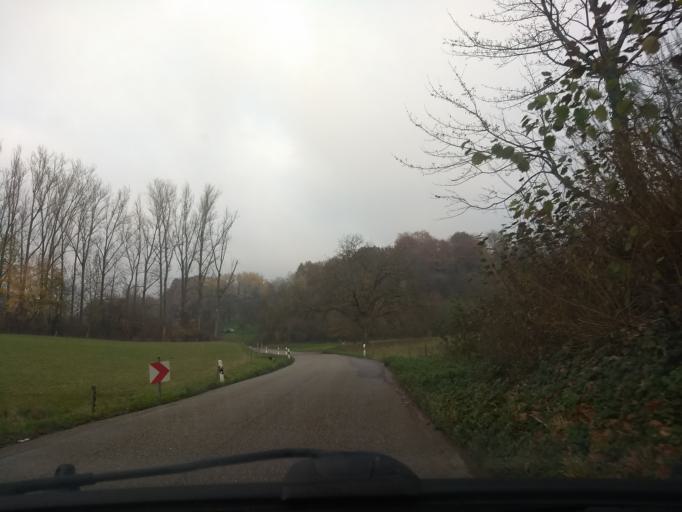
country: DE
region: Baden-Wuerttemberg
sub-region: Karlsruhe Region
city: Baden-Baden
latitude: 48.7929
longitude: 8.2156
